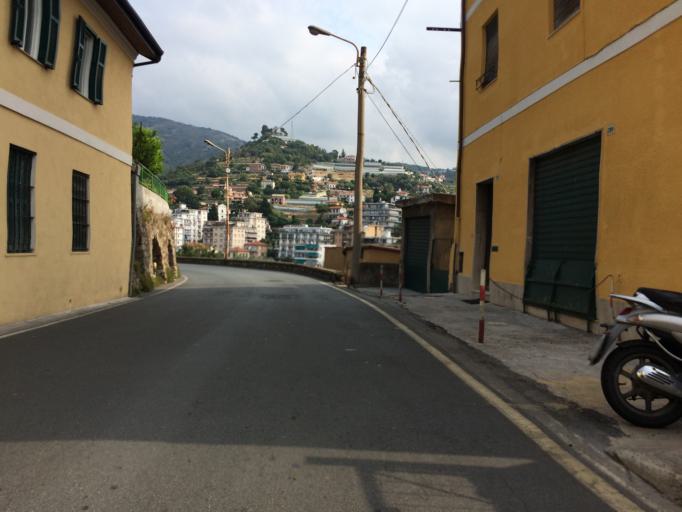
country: IT
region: Liguria
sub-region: Provincia di Imperia
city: San Remo
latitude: 43.8240
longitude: 7.7725
